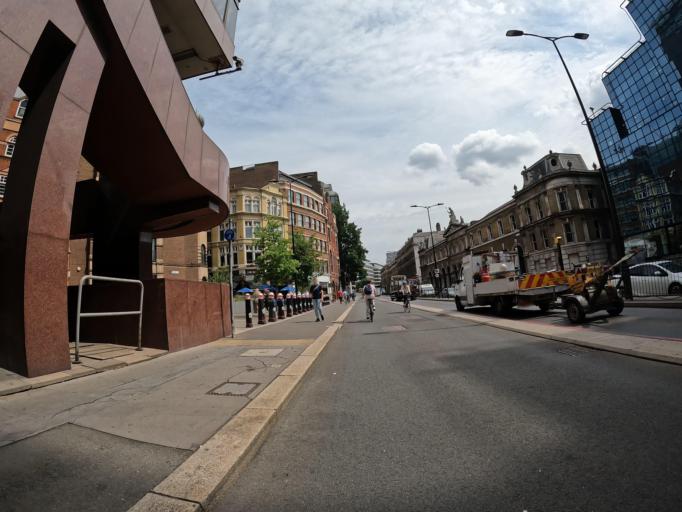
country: GB
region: England
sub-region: Greater London
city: Blackheath
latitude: 51.4841
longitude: 0.0060
